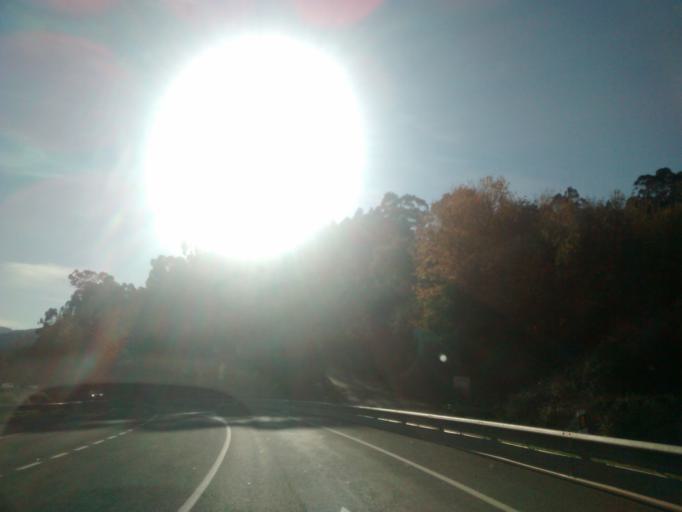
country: ES
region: Cantabria
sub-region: Provincia de Cantabria
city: Puente Viesgo
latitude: 43.3179
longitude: -3.9626
